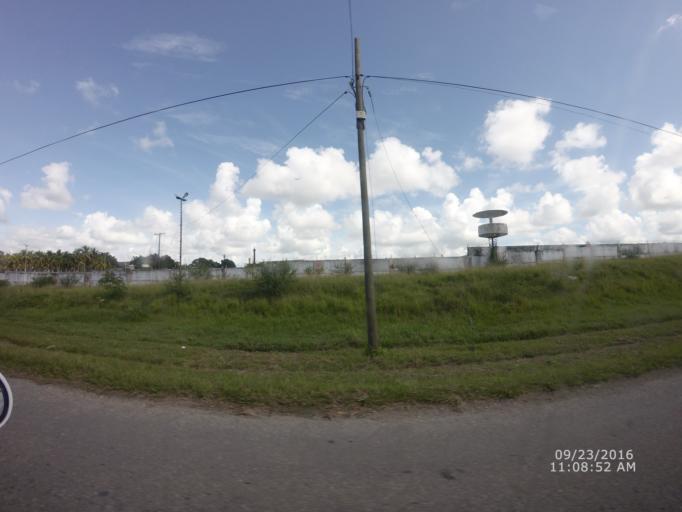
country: CU
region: La Habana
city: Arroyo Naranjo
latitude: 23.0157
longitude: -82.2364
